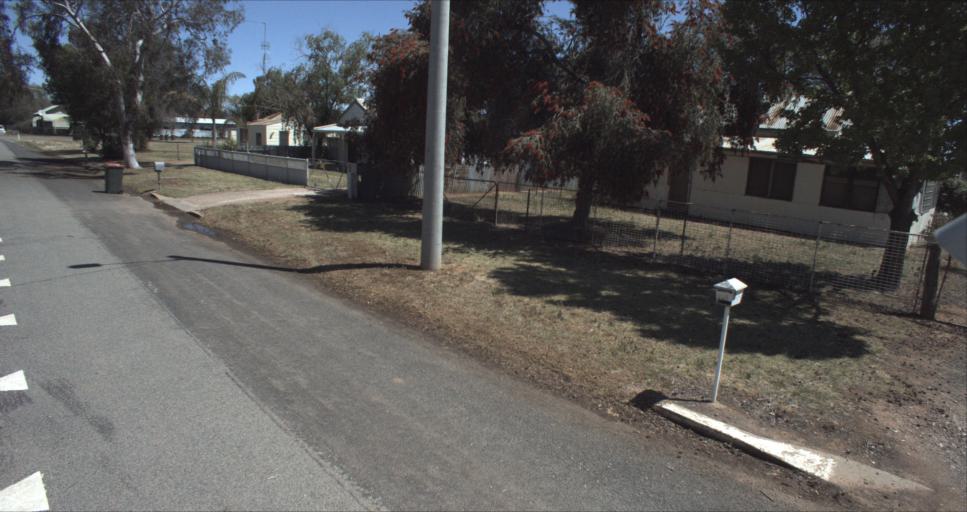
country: AU
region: New South Wales
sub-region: Leeton
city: Leeton
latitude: -34.5242
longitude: 146.3312
